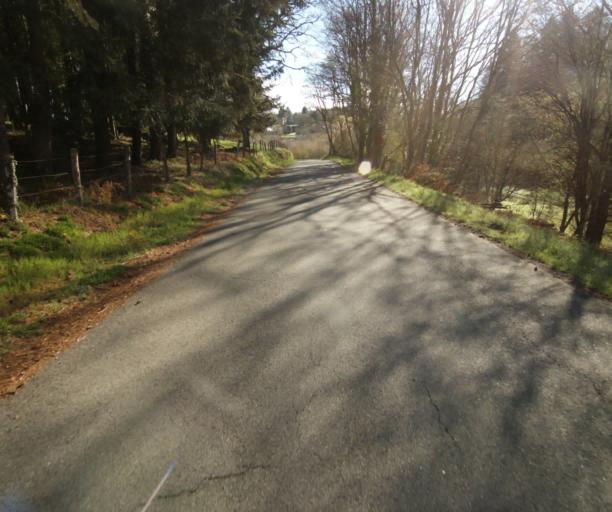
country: FR
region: Limousin
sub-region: Departement de la Correze
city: Laguenne
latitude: 45.2675
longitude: 1.8678
